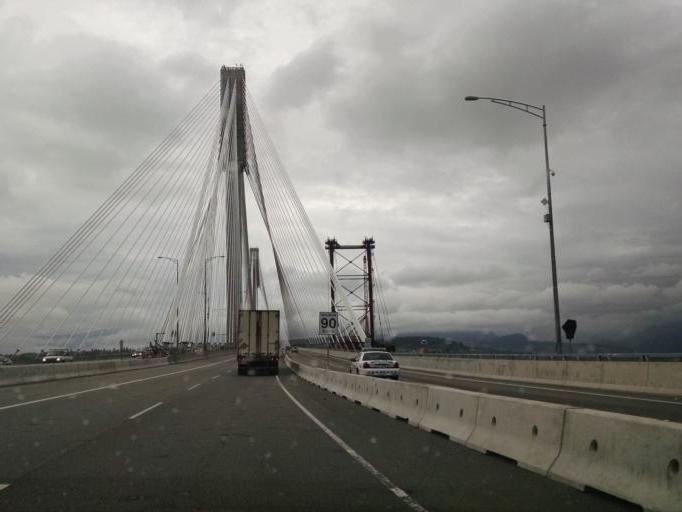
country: CA
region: British Columbia
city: Port Moody
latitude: 49.2134
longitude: -122.8104
